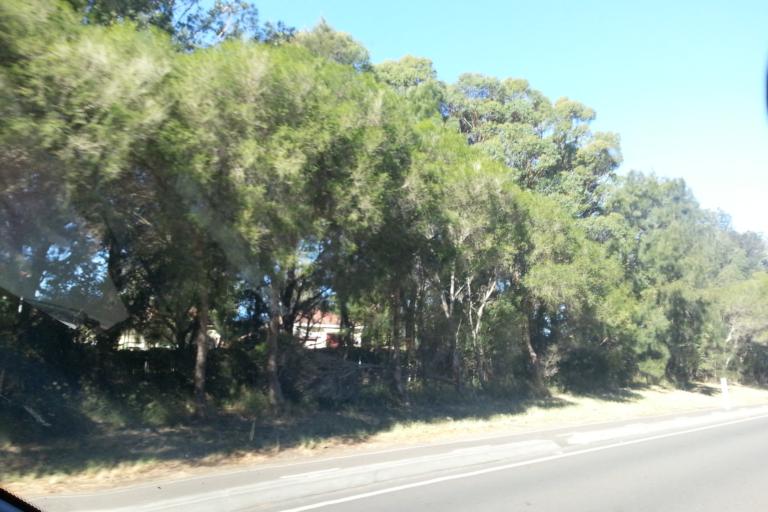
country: AU
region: New South Wales
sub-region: Wollongong
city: Koonawarra
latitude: -34.4870
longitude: 150.7990
